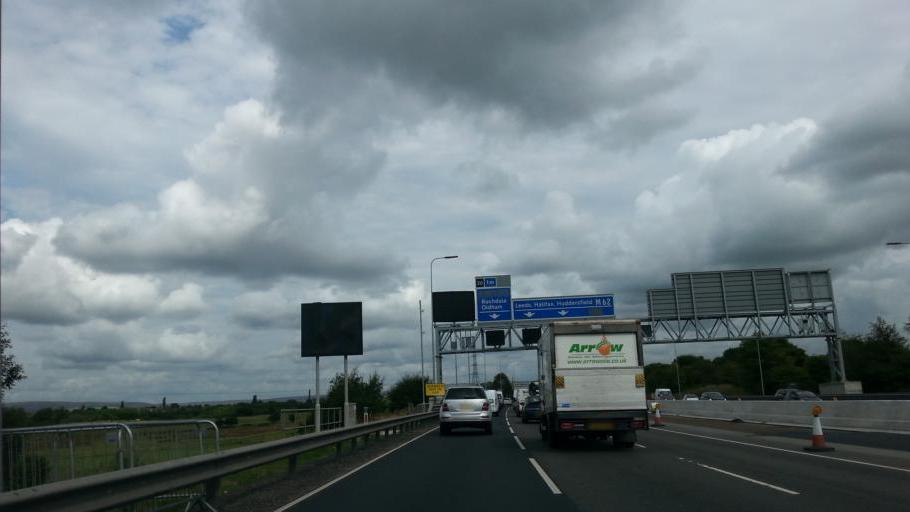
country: GB
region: England
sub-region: Manchester
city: Heywood
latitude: 53.5813
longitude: -2.1974
